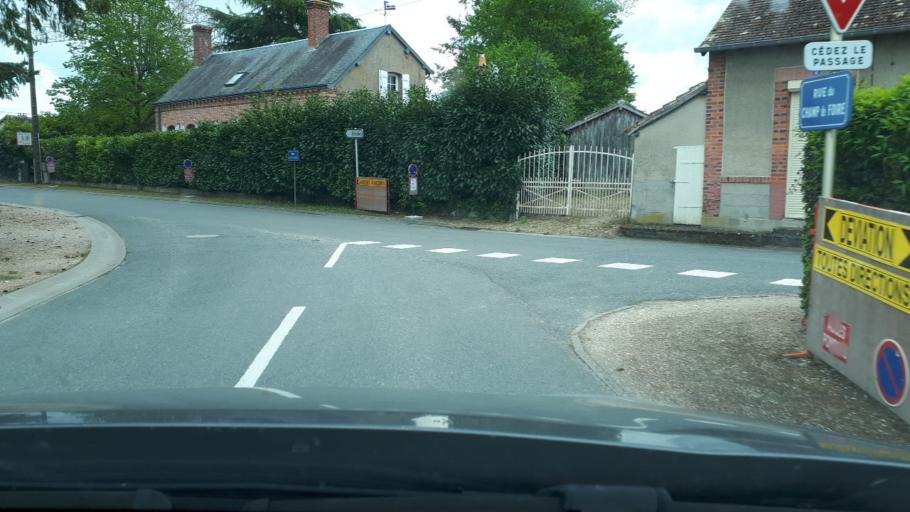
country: FR
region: Centre
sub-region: Departement du Loir-et-Cher
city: Souesmes
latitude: 47.5106
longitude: 2.1514
